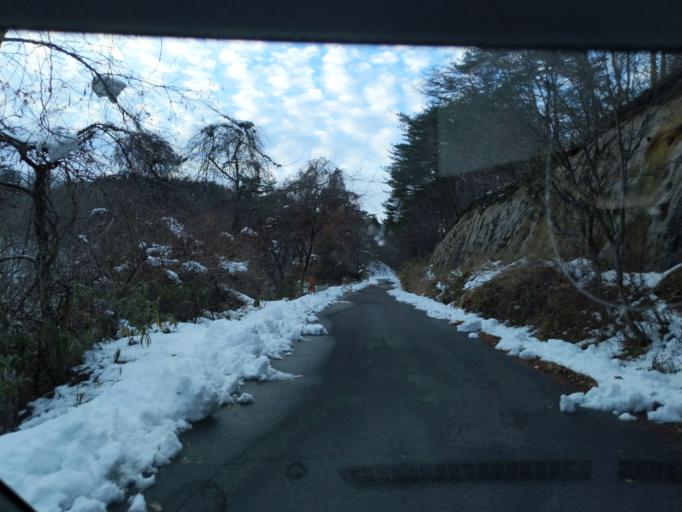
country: JP
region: Iwate
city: Mizusawa
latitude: 39.0412
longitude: 141.0292
